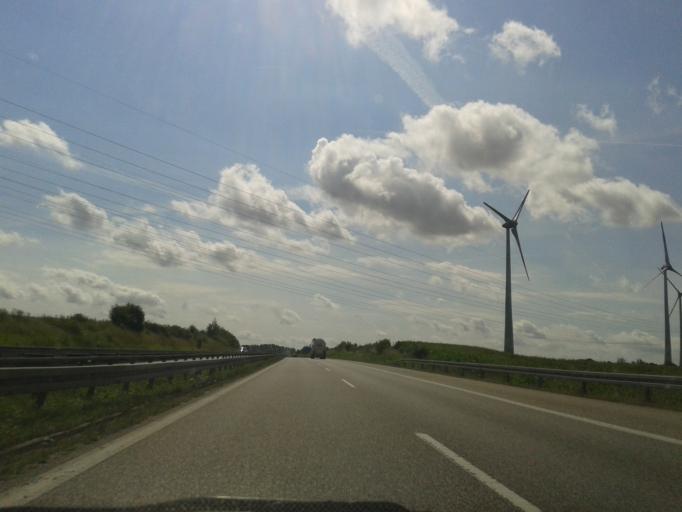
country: DE
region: Brandenburg
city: Schonfeld
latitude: 53.4615
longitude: 13.9661
